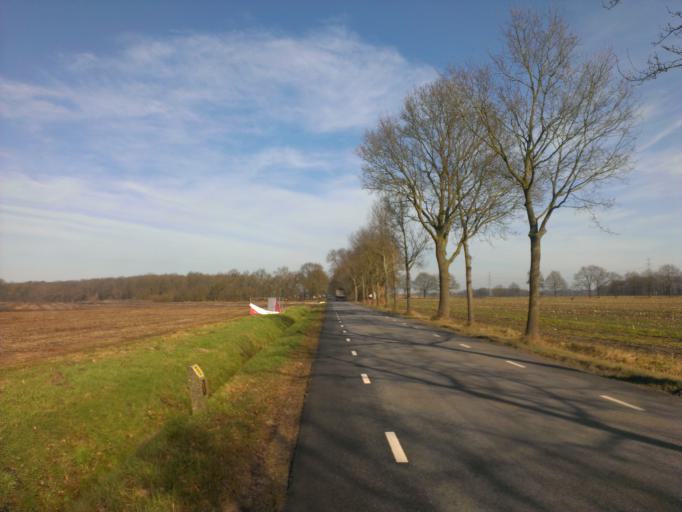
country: NL
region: Drenthe
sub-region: Gemeente Hoogeveen
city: Hoogeveen
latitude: 52.7426
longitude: 6.4749
